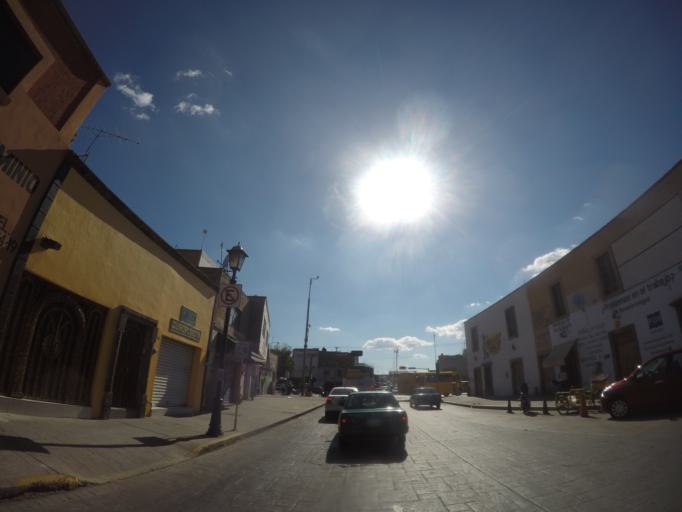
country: MX
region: San Luis Potosi
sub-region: San Luis Potosi
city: San Luis Potosi
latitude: 22.1581
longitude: -100.9741
